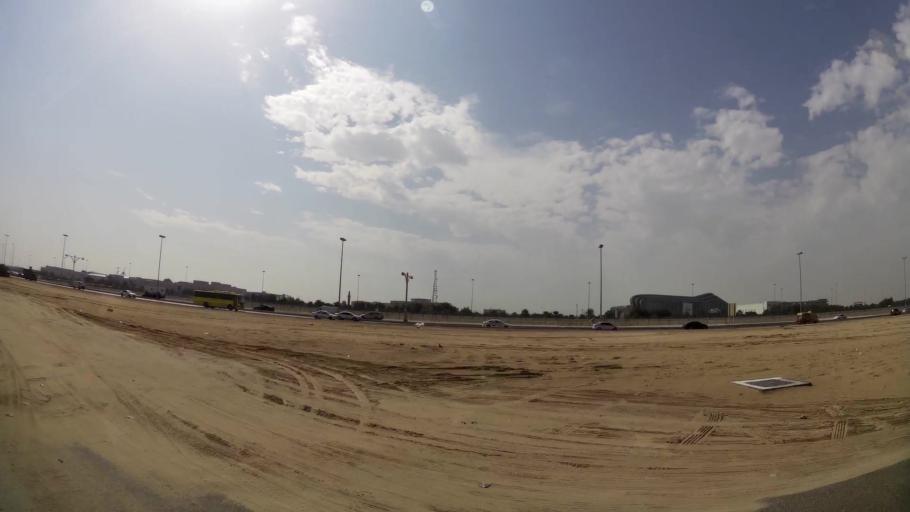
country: AE
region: Abu Dhabi
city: Abu Dhabi
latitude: 24.3401
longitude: 54.5299
